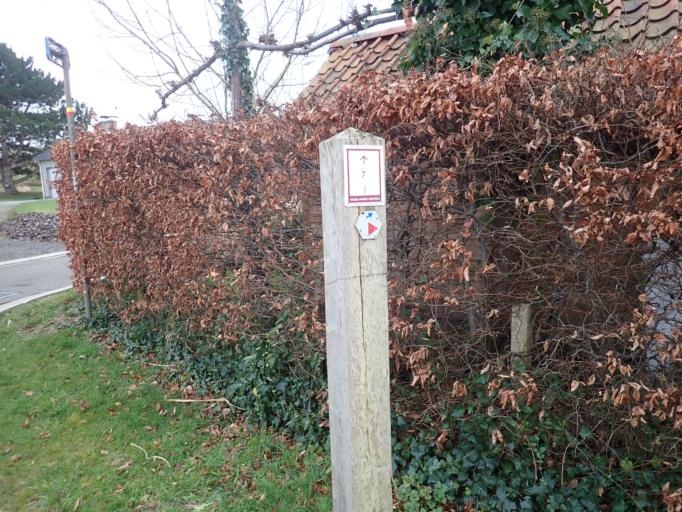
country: BE
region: Flanders
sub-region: Provincie Vlaams-Brabant
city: Aarschot
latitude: 50.9626
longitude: 4.7962
